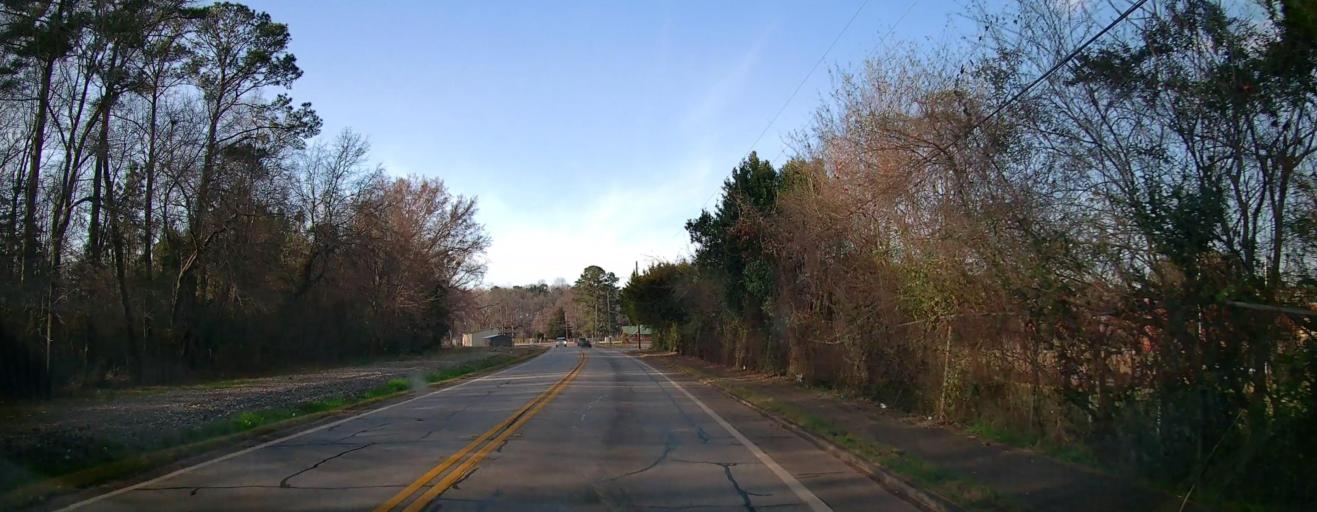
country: US
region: Georgia
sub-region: Harris County
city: Hamilton
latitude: 32.7488
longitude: -84.8699
